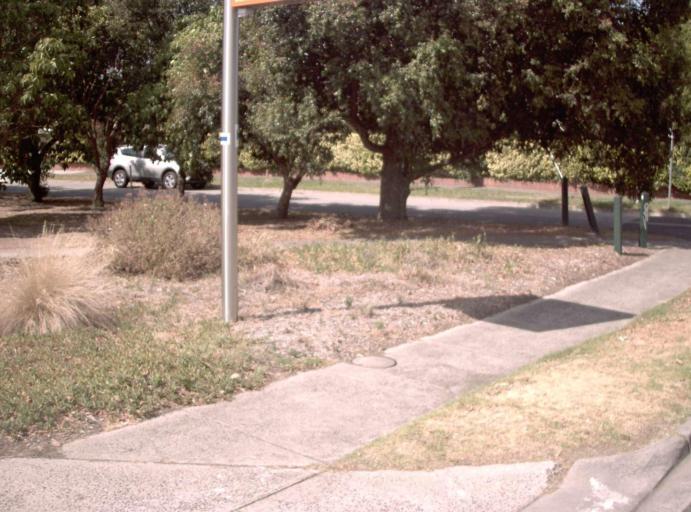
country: AU
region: Victoria
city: Carnegie
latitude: -37.8799
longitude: 145.0719
